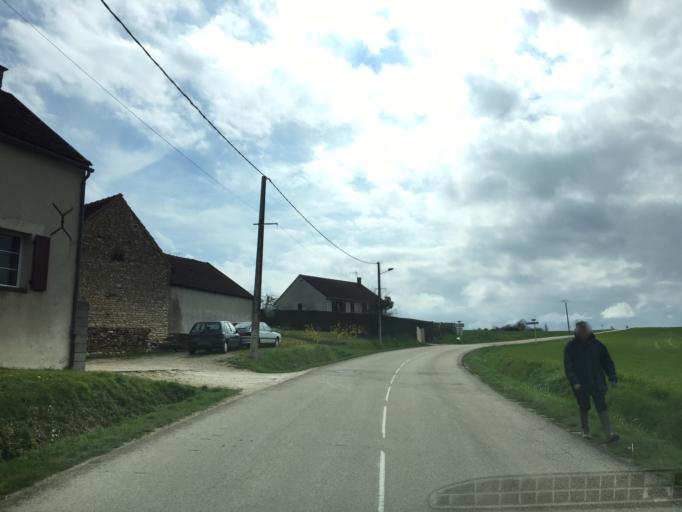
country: FR
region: Bourgogne
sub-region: Departement de l'Yonne
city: Pourrain
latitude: 47.7985
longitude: 3.4167
